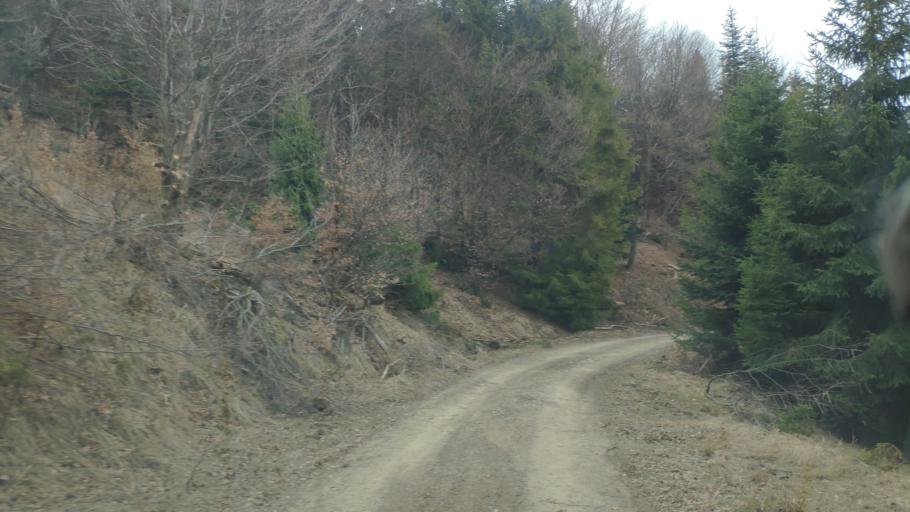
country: SK
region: Kosicky
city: Gelnica
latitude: 48.7590
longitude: 21.0398
